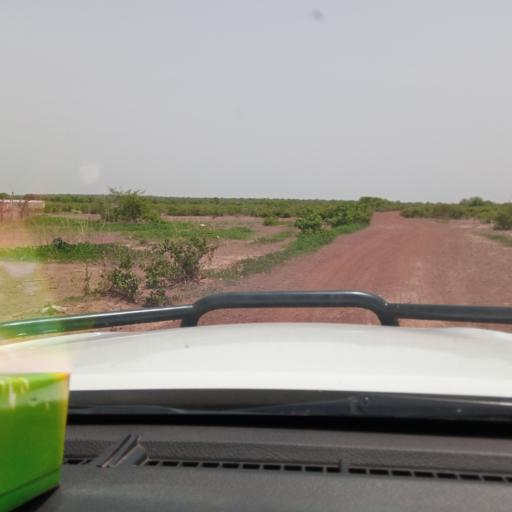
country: ML
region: Koulikoro
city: Koulikoro
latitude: 13.1088
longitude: -7.6142
